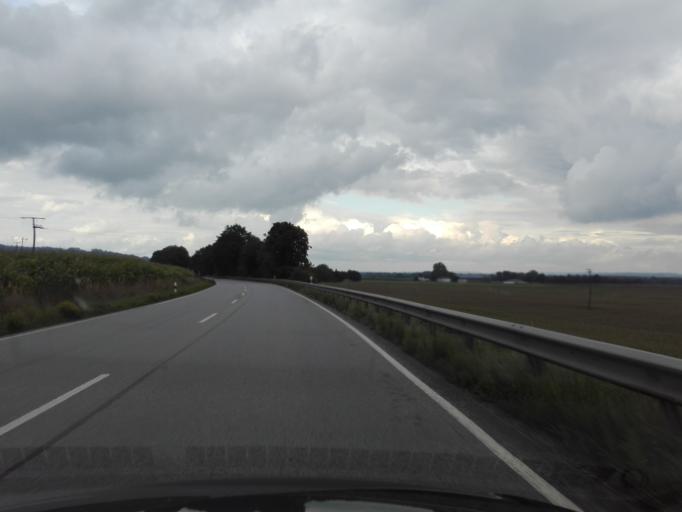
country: DE
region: Bavaria
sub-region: Lower Bavaria
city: Stubenberg
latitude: 48.2937
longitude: 13.1116
